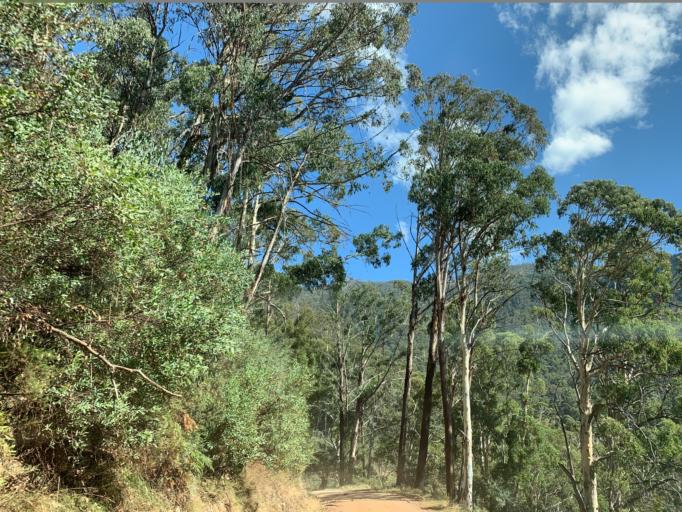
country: AU
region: Victoria
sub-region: Mansfield
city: Mansfield
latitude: -37.1005
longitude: 146.5041
